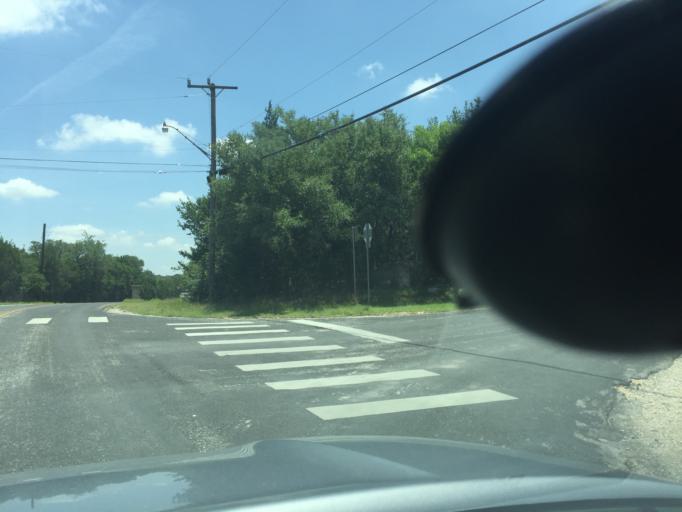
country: US
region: Texas
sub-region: Bexar County
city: Timberwood Park
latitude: 29.7058
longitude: -98.5093
